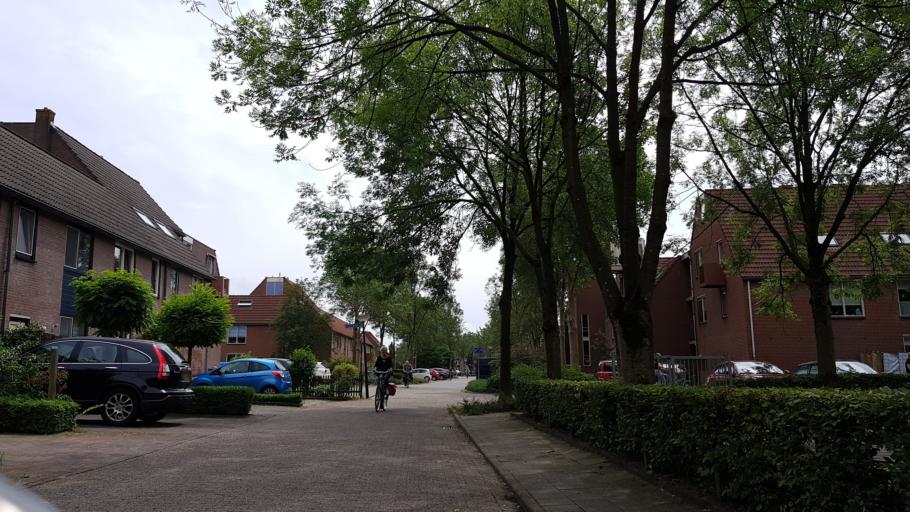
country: NL
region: Gelderland
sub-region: Gemeente Apeldoorn
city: Apeldoorn
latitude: 52.1986
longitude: 6.0008
